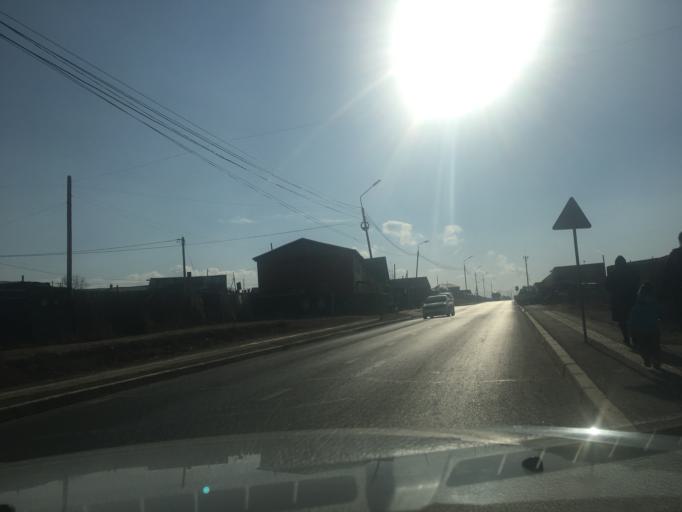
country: MN
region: Ulaanbaatar
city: Ulaanbaatar
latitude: 47.9648
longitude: 106.8289
